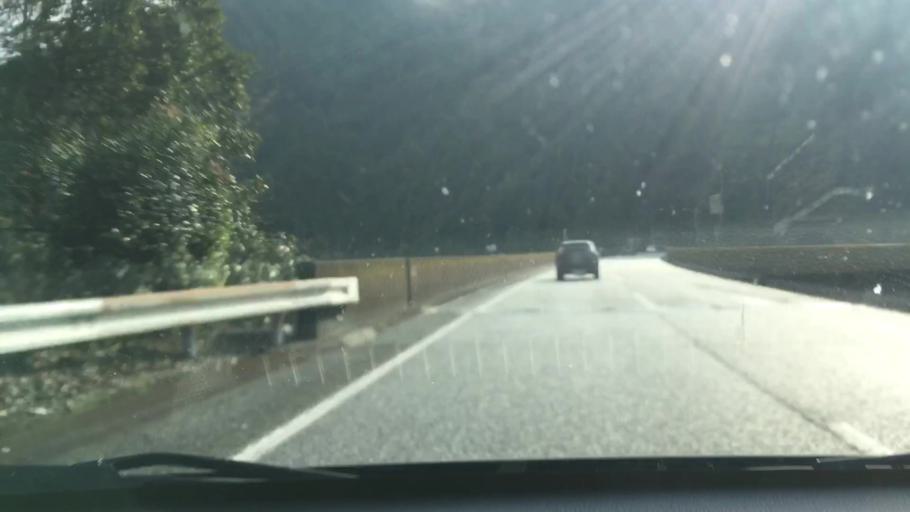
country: JP
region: Kumamoto
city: Yatsushiro
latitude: 32.4261
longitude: 130.7024
